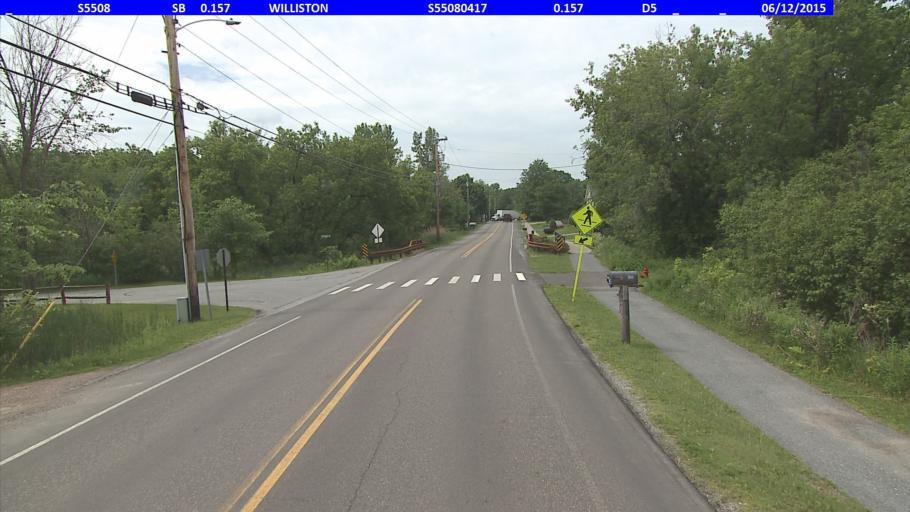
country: US
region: Vermont
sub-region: Chittenden County
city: Williston
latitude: 44.4393
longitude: -73.0664
